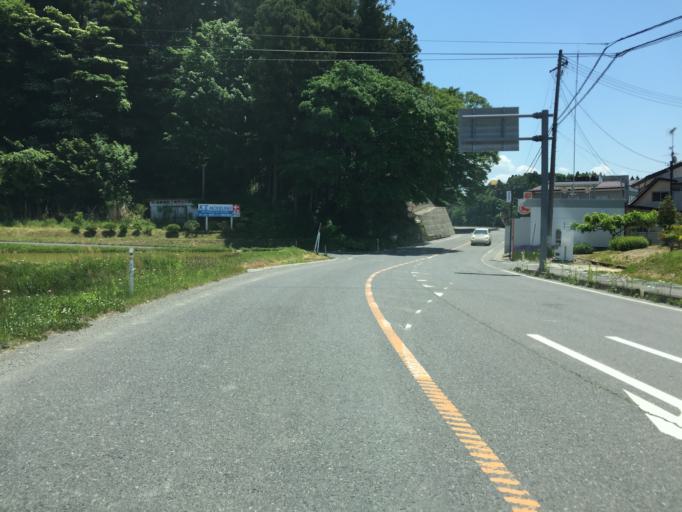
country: JP
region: Fukushima
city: Motomiya
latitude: 37.5024
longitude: 140.4574
